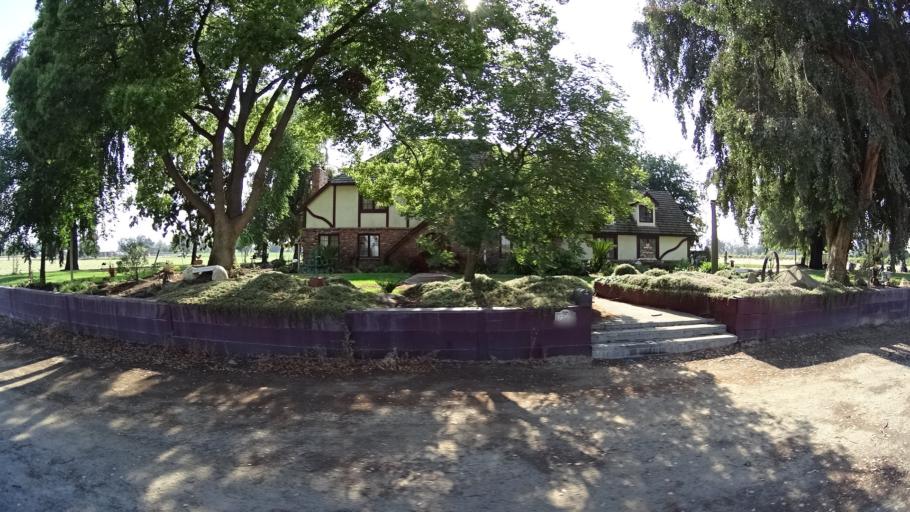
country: US
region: California
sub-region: Kings County
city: Lemoore
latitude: 36.3637
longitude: -119.8161
